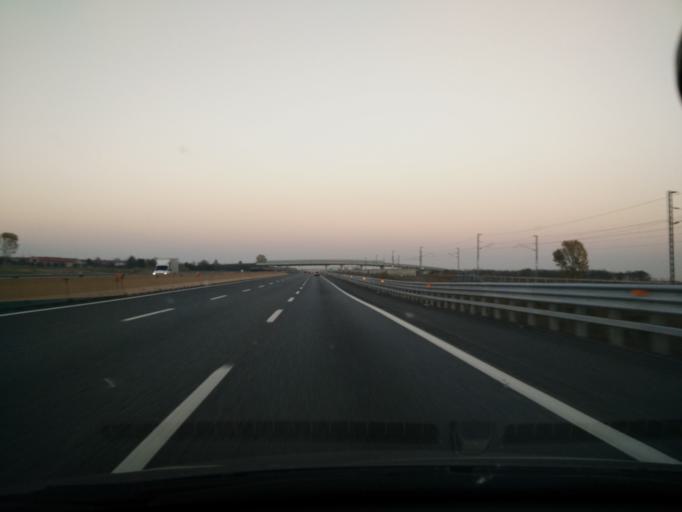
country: IT
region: Piedmont
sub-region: Provincia di Vercelli
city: Saluggia
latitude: 45.2606
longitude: 8.0070
